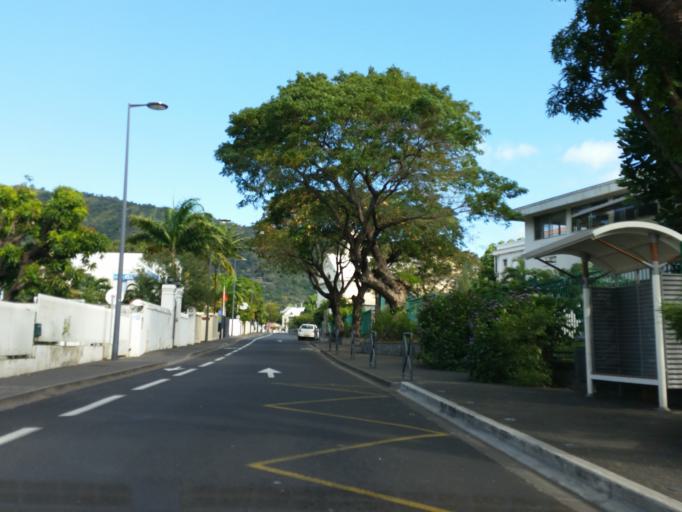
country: RE
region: Reunion
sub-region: Reunion
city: Saint-Denis
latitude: -20.8856
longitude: 55.4539
